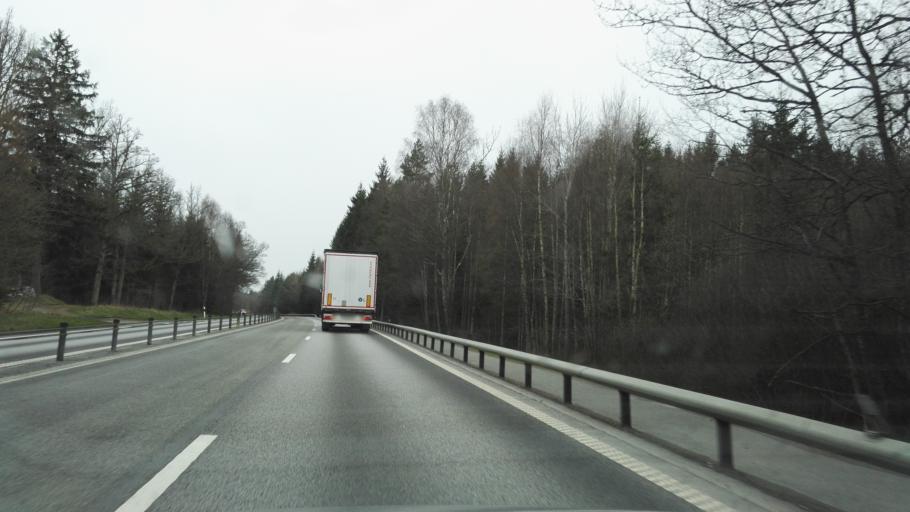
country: SE
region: Skane
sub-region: Osby Kommun
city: Osby
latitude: 56.3603
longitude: 14.0154
